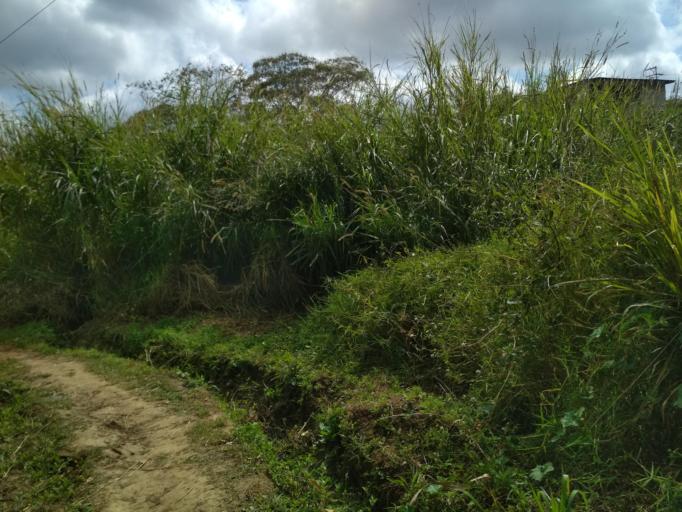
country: MX
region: Veracruz
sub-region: Emiliano Zapata
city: Jacarandas
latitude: 19.4981
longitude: -96.8357
